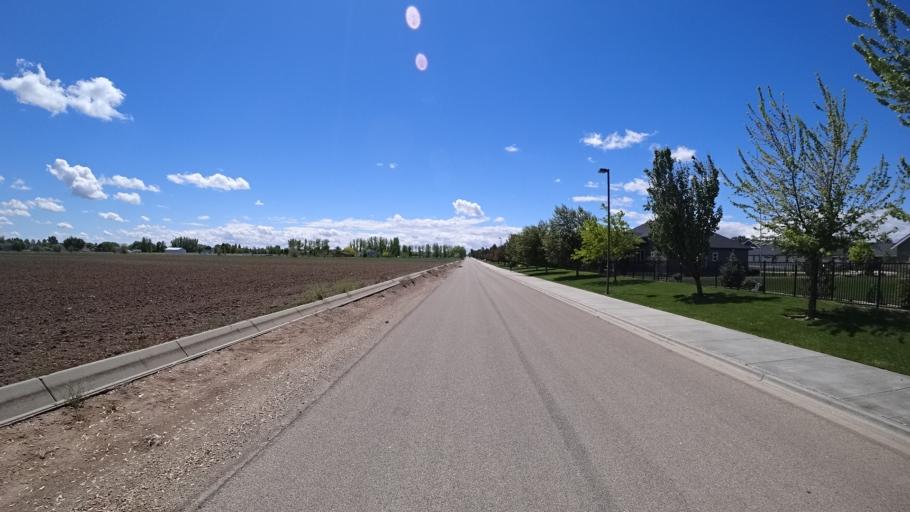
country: US
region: Idaho
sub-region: Ada County
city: Kuna
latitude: 43.5089
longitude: -116.4237
